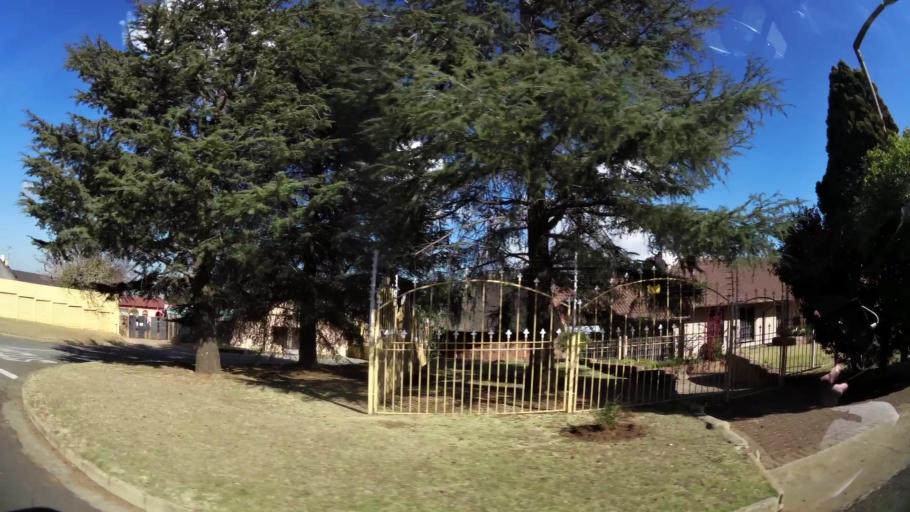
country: ZA
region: Gauteng
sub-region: City of Johannesburg Metropolitan Municipality
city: Roodepoort
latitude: -26.1406
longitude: 27.8224
